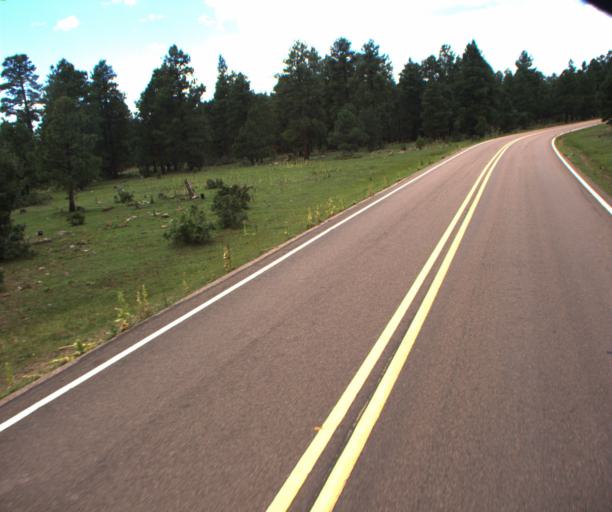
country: US
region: Arizona
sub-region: Navajo County
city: Pinetop-Lakeside
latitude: 34.0149
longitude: -109.7785
